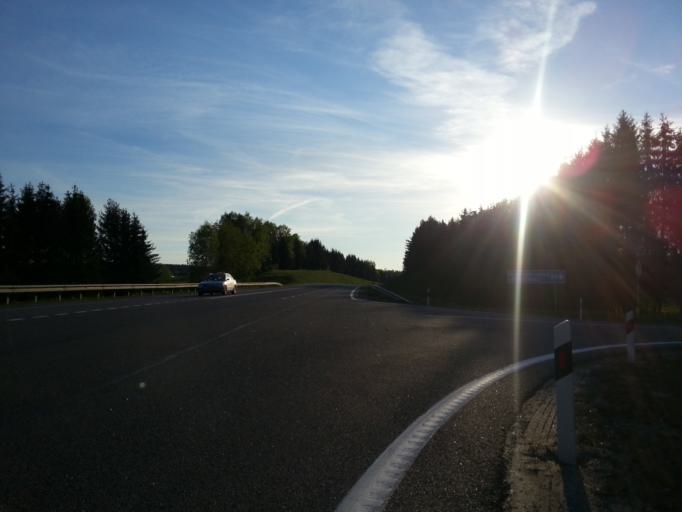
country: BY
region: Minsk
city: Slabada
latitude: 54.0342
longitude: 27.8540
